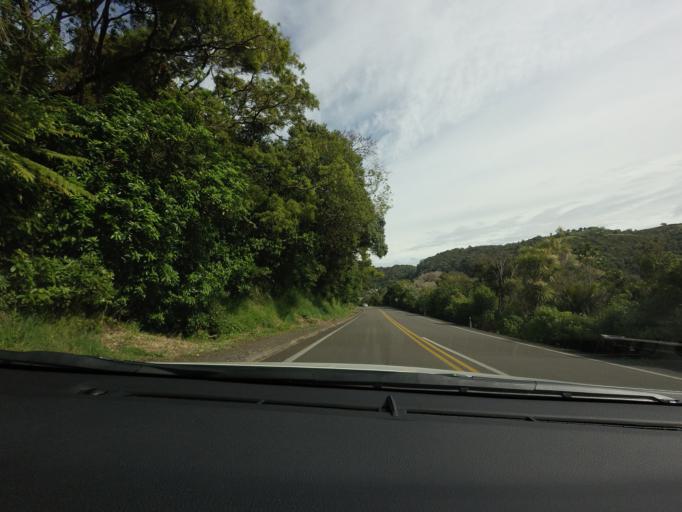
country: NZ
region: Auckland
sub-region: Auckland
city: Warkworth
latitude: -36.5385
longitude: 174.7047
